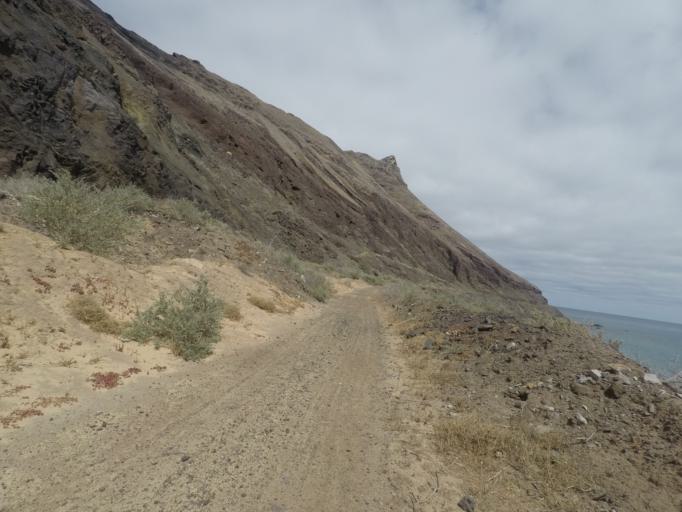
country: PT
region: Madeira
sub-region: Porto Santo
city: Vila de Porto Santo
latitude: 33.0626
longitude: -16.3040
